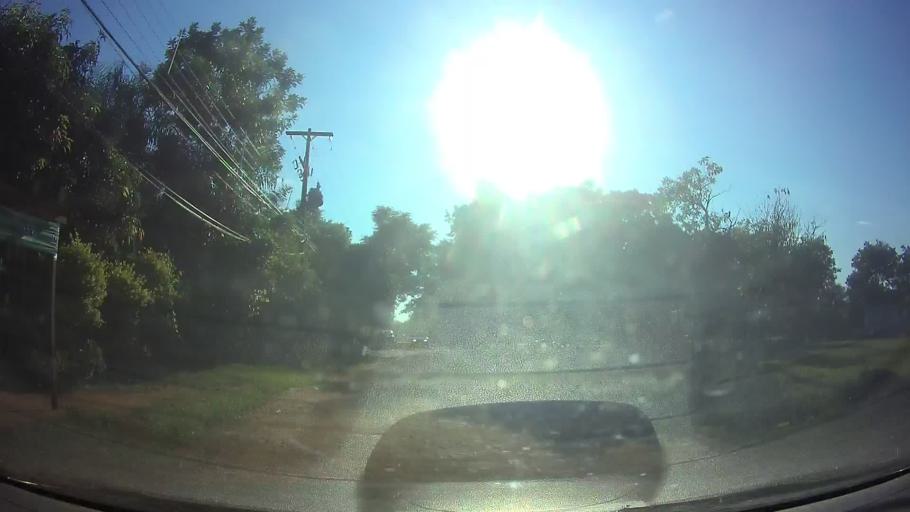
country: PY
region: Central
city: San Lorenzo
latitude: -25.2571
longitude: -57.4713
